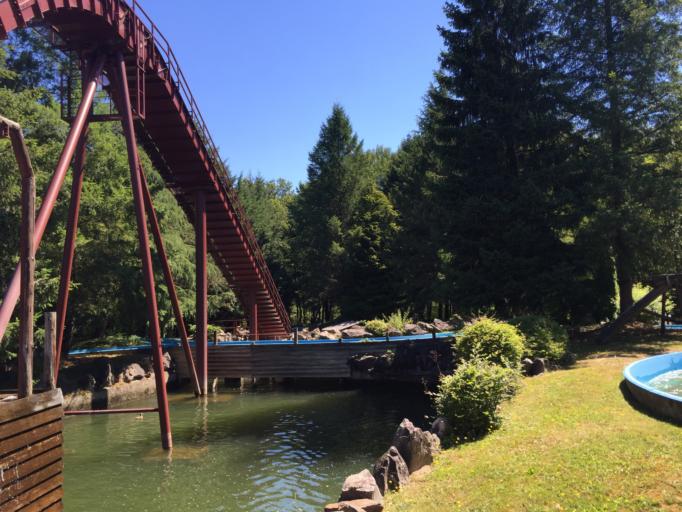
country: FR
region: Auvergne
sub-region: Departement de l'Allier
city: Dompierre-sur-Besbre
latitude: 46.5092
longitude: 3.6332
